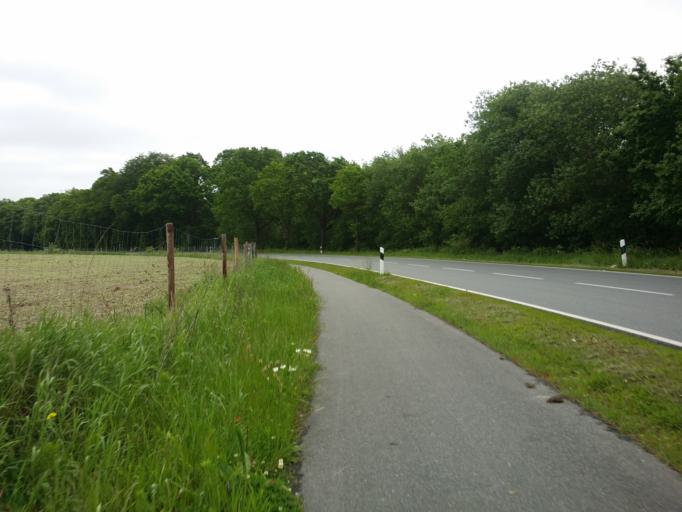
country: DE
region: Lower Saxony
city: Rastede
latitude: 53.2184
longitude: 8.2541
